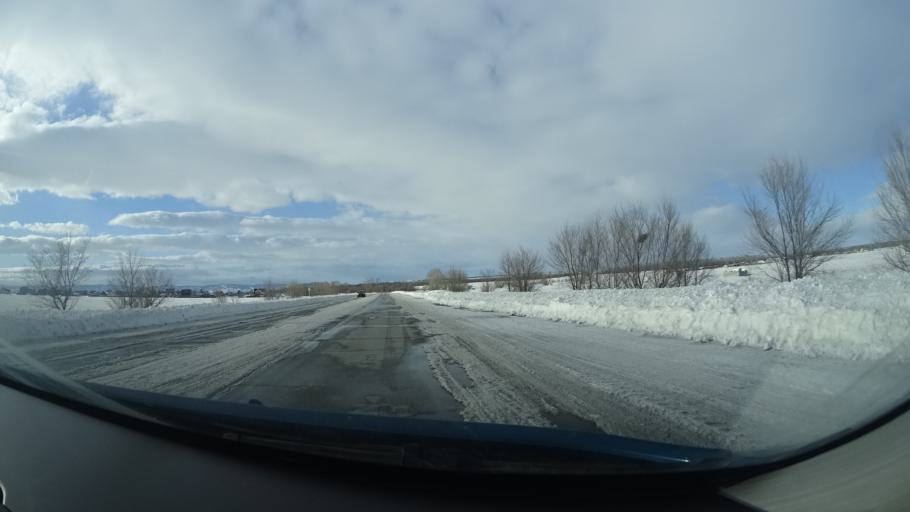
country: RU
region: Chelyabinsk
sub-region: Gorod Magnitogorsk
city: Magnitogorsk
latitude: 53.5885
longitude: 58.8788
